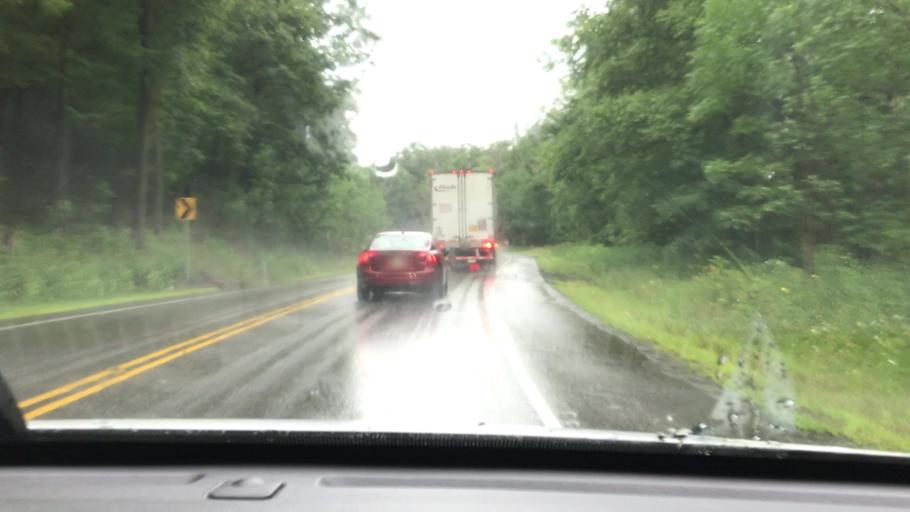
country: US
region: Pennsylvania
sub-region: Clearfield County
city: Osceola Mills
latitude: 40.7770
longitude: -78.2378
